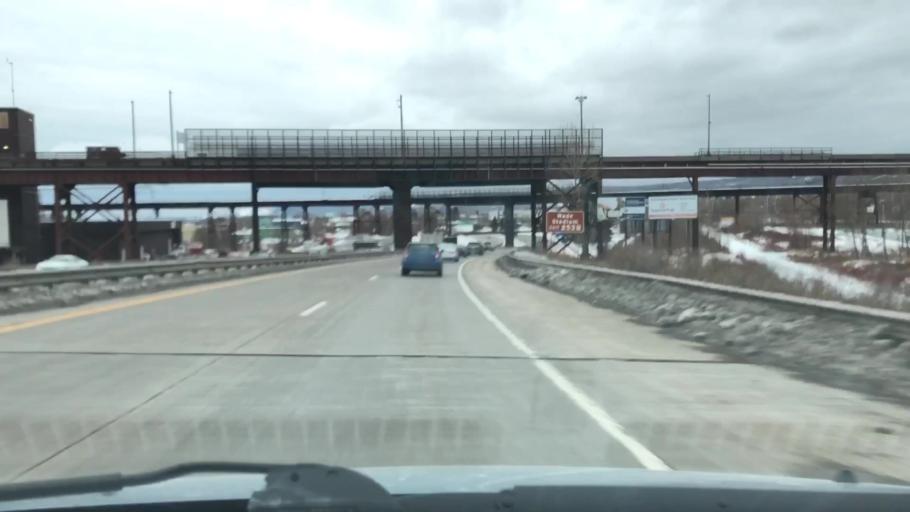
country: US
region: Minnesota
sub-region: Saint Louis County
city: Duluth
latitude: 46.7543
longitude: -92.1359
